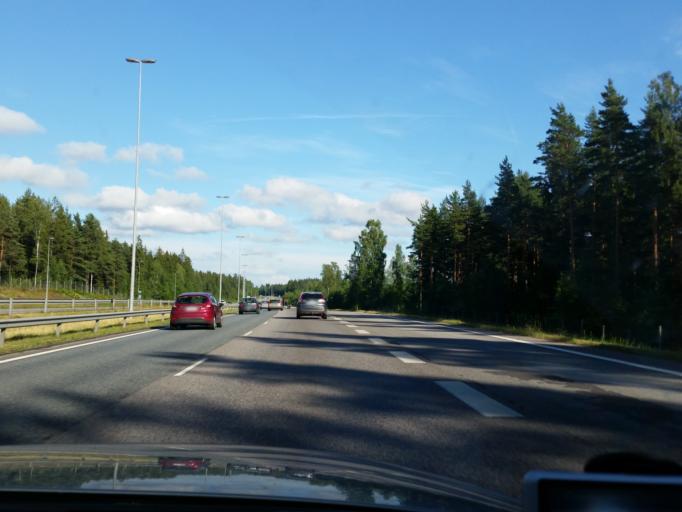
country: FI
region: Uusimaa
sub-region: Helsinki
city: Kirkkonummi
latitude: 60.2723
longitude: 24.4572
